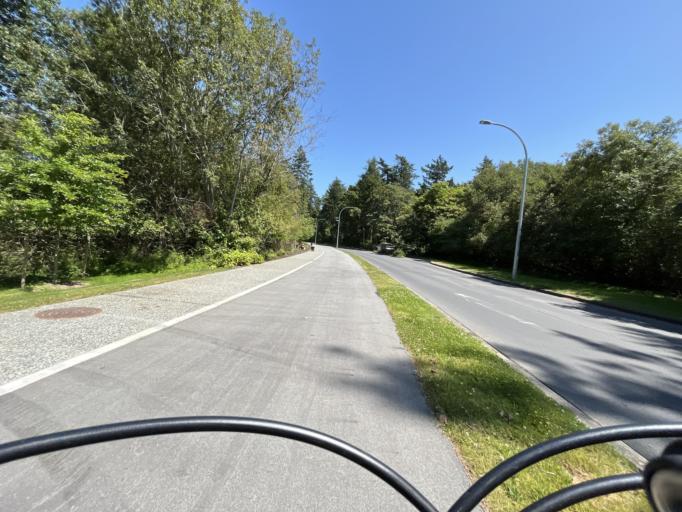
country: CA
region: British Columbia
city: Oak Bay
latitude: 48.4605
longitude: -123.3136
